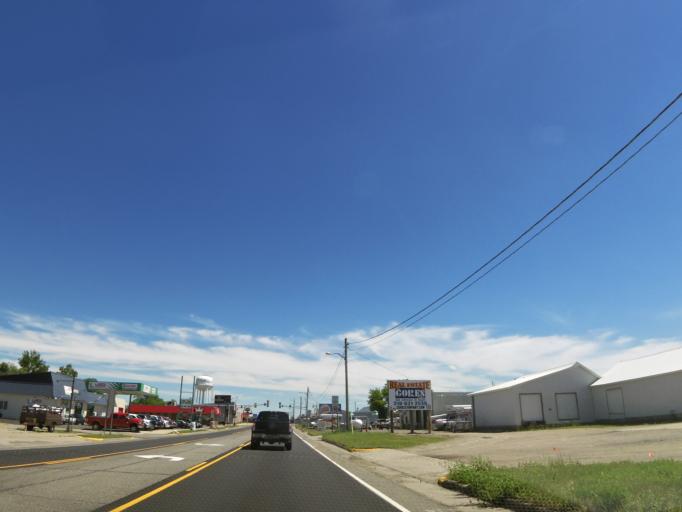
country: US
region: Minnesota
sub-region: Wadena County
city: Wadena
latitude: 46.4439
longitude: -95.1409
